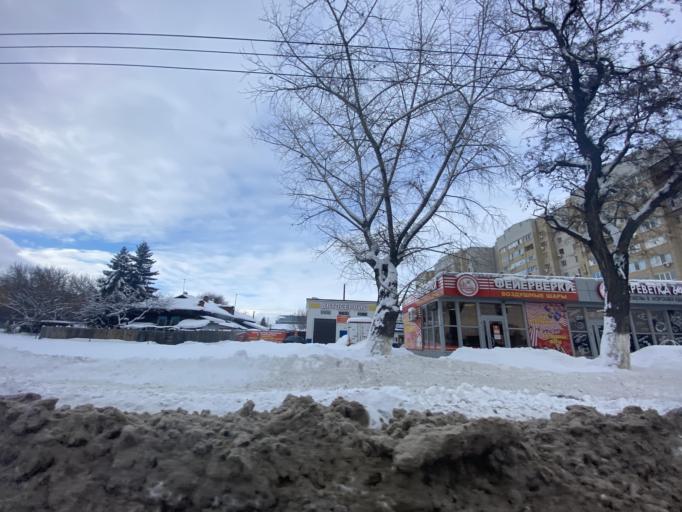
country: RU
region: Saratov
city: Engel's
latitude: 51.4975
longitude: 46.0948
